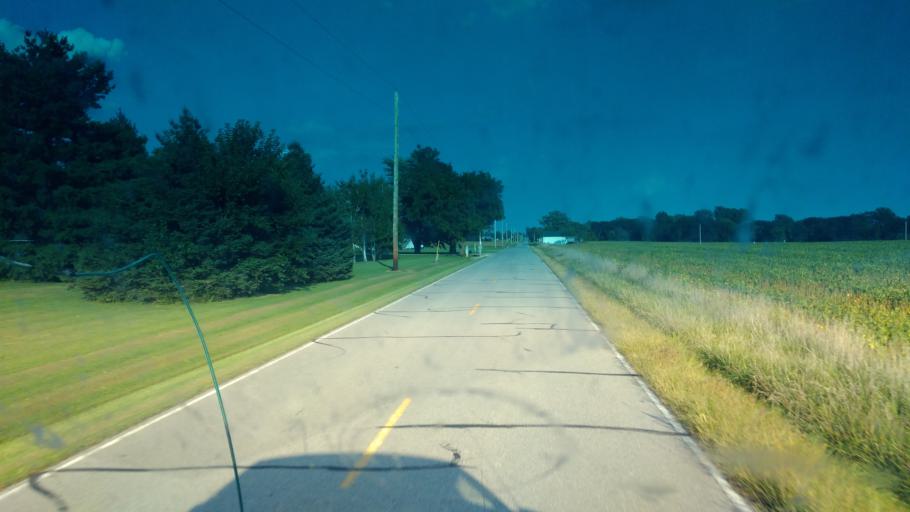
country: US
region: Ohio
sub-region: Crawford County
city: Bucyrus
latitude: 40.9651
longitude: -83.0589
